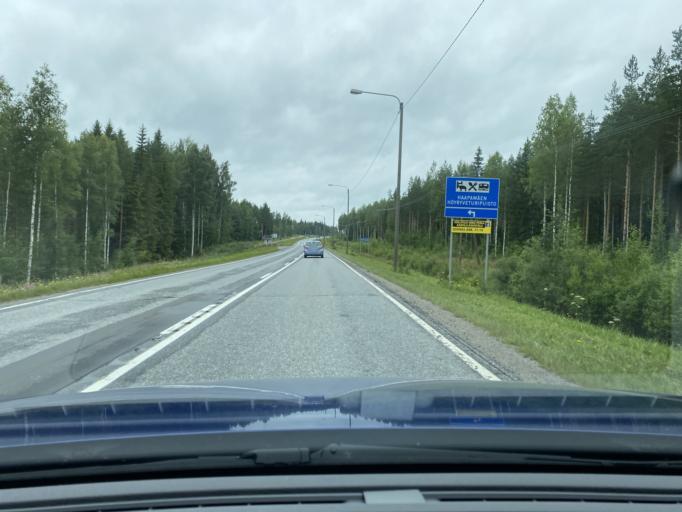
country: FI
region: Central Finland
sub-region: Keuruu
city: Keuruu
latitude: 62.2409
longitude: 24.4861
